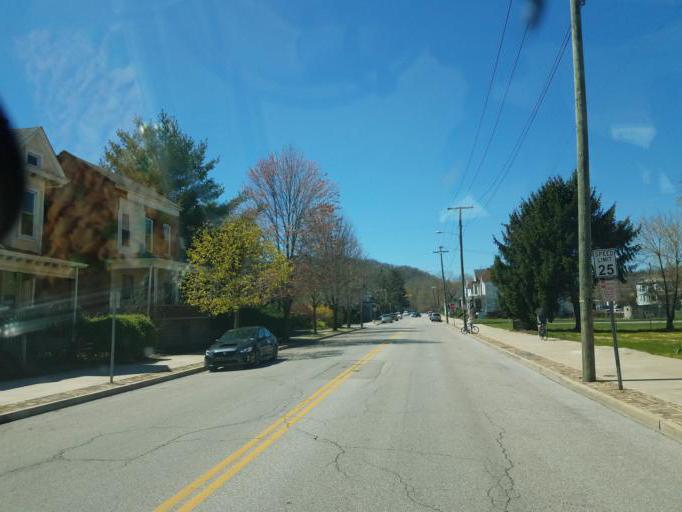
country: US
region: Ohio
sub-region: Belmont County
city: Bridgeport
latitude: 40.0696
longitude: -80.7328
